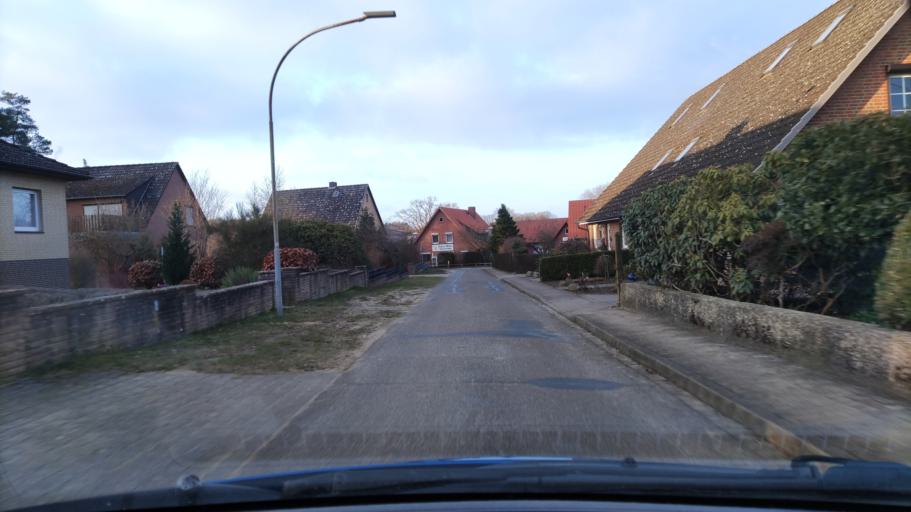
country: DE
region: Lower Saxony
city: Gerdau
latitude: 52.9693
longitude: 10.3880
